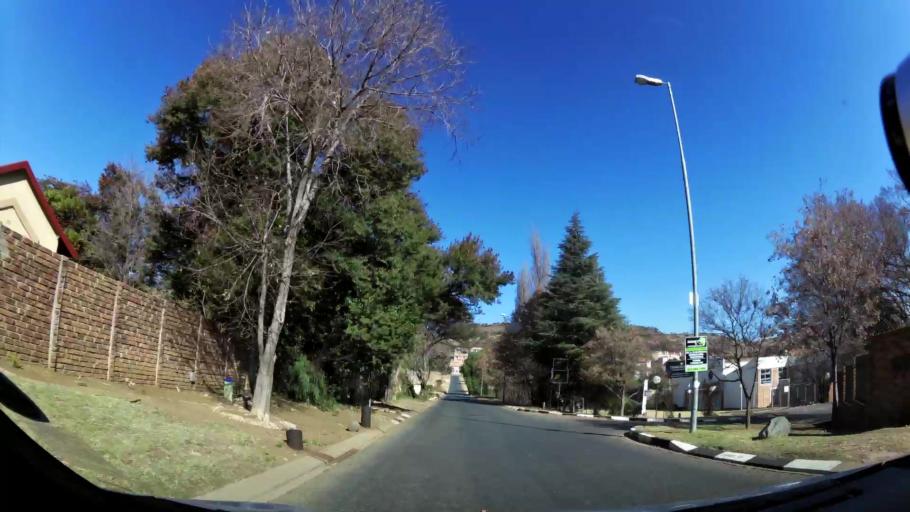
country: ZA
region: Gauteng
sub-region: City of Johannesburg Metropolitan Municipality
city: Johannesburg
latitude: -26.2754
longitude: 28.0238
